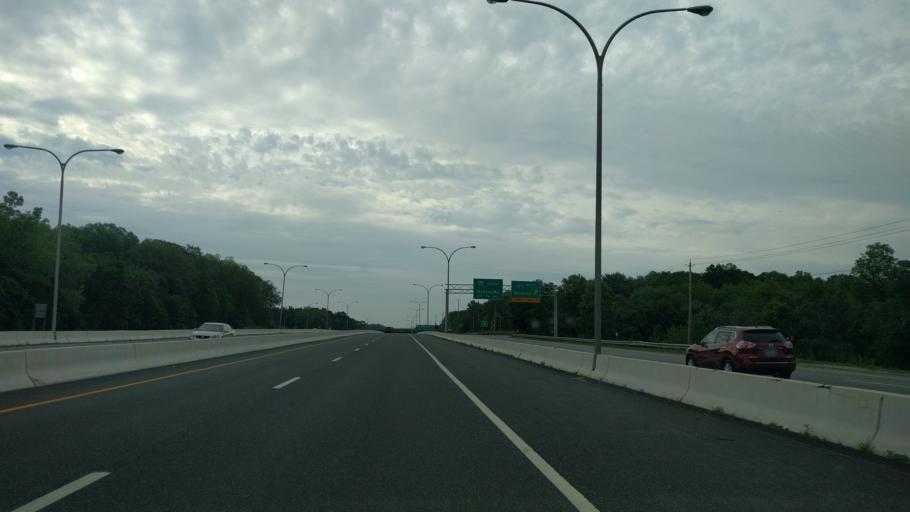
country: US
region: Rhode Island
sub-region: Providence County
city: Cumberland Hill
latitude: 41.9472
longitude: -71.4814
